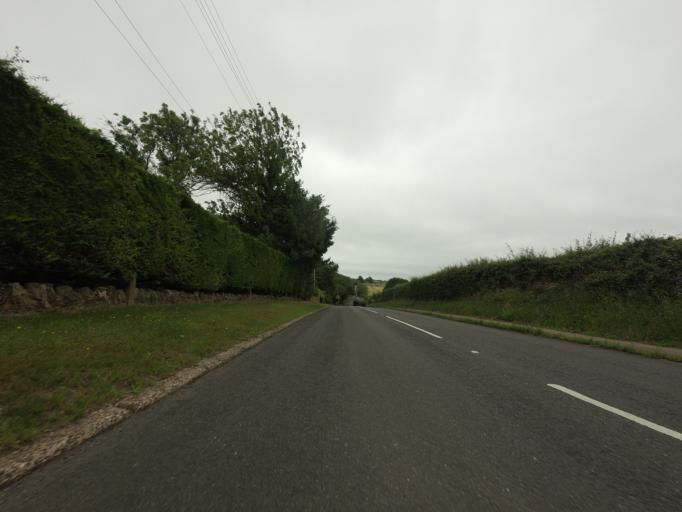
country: GB
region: England
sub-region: Kent
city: Meopham
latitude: 51.3840
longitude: 0.3440
